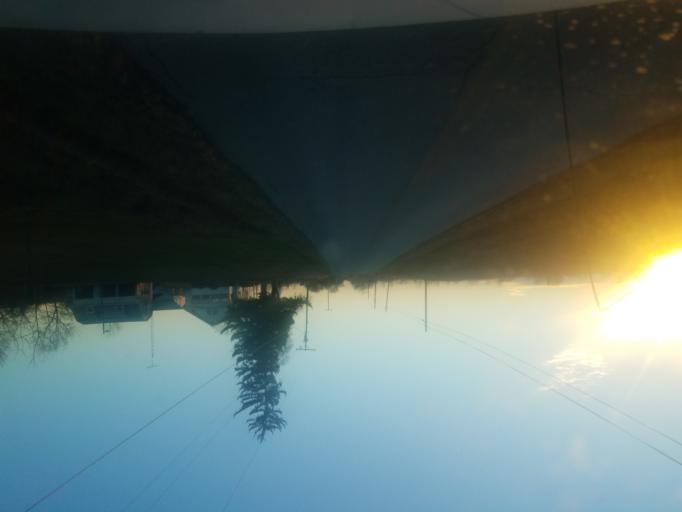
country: US
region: Ohio
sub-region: Richland County
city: Ontario
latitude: 40.8431
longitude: -82.5653
